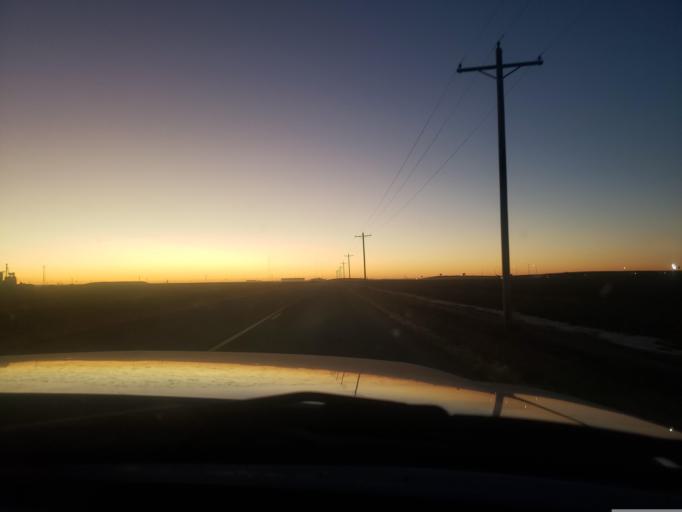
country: US
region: Kansas
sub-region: Finney County
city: Garden City
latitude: 38.0008
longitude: -100.8766
